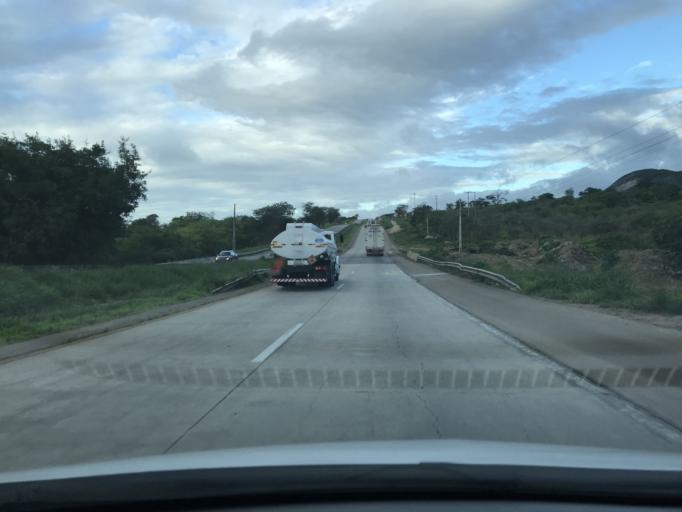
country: BR
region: Pernambuco
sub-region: Caruaru
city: Caruaru
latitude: -8.3007
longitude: -35.9122
